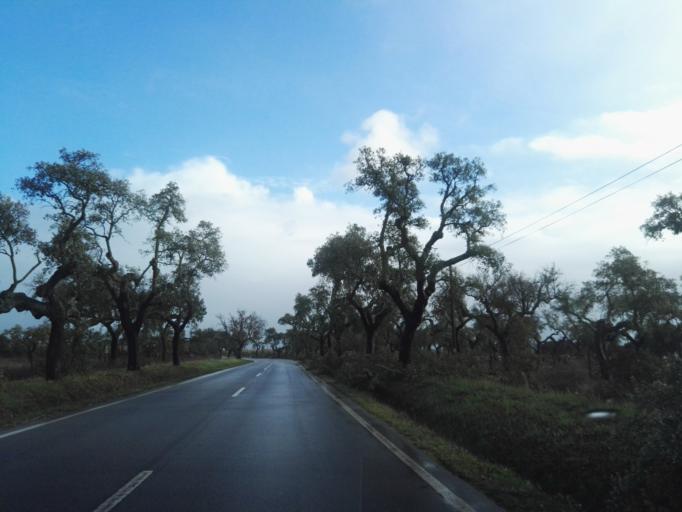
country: PT
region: Portalegre
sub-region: Elvas
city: Elvas
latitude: 38.9350
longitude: -7.1903
